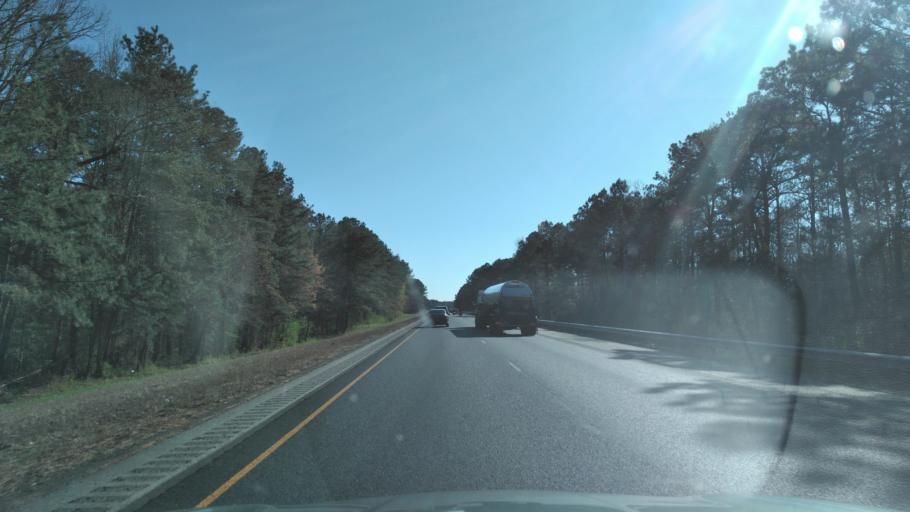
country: US
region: Alabama
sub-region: Butler County
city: Greenville
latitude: 31.7520
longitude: -86.7076
